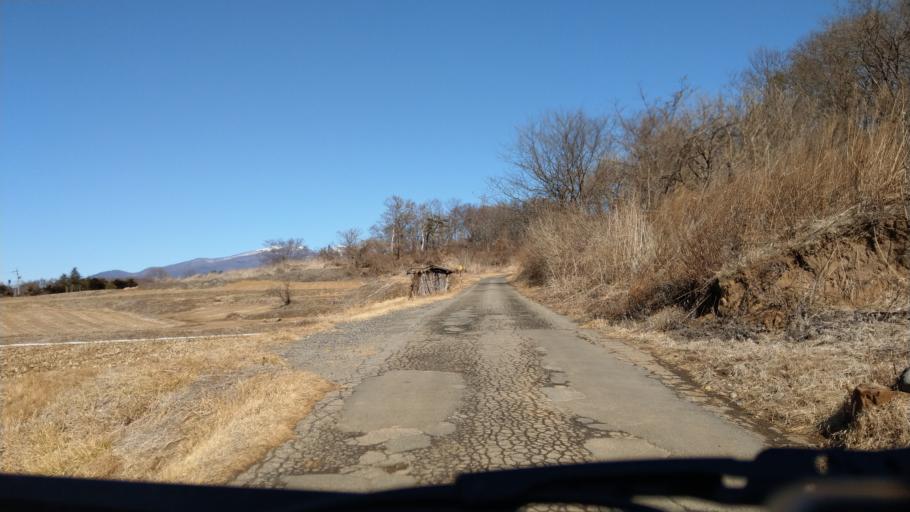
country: JP
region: Nagano
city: Komoro
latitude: 36.3140
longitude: 138.4010
